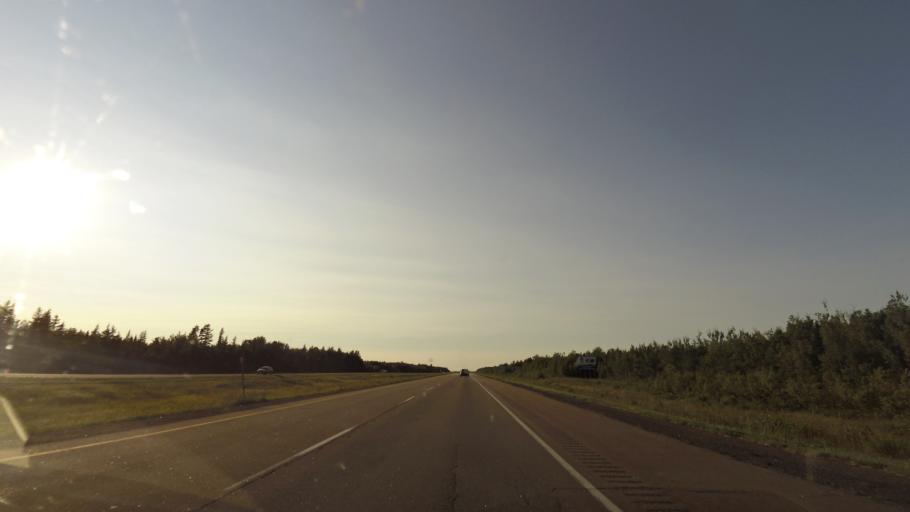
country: CA
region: New Brunswick
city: Dieppe
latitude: 46.1107
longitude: -64.6132
